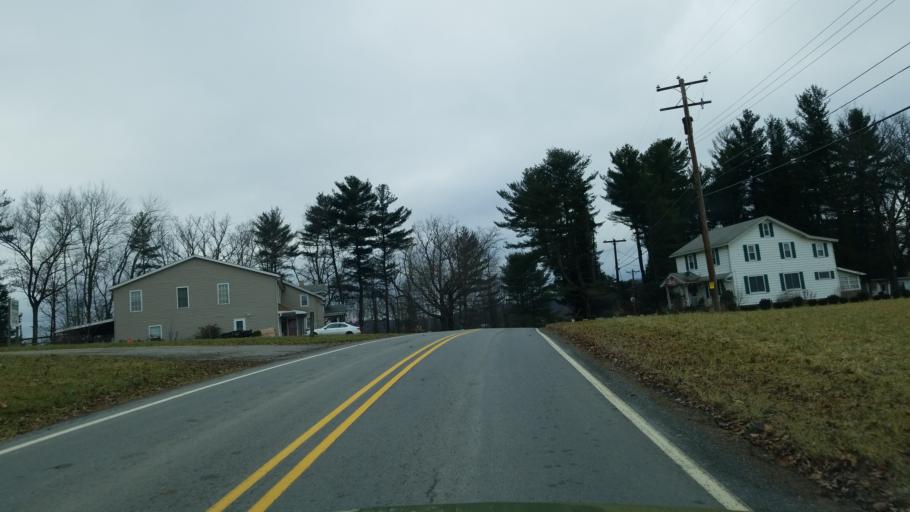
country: US
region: Pennsylvania
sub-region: Clearfield County
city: Hyde
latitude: 41.0325
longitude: -78.4752
